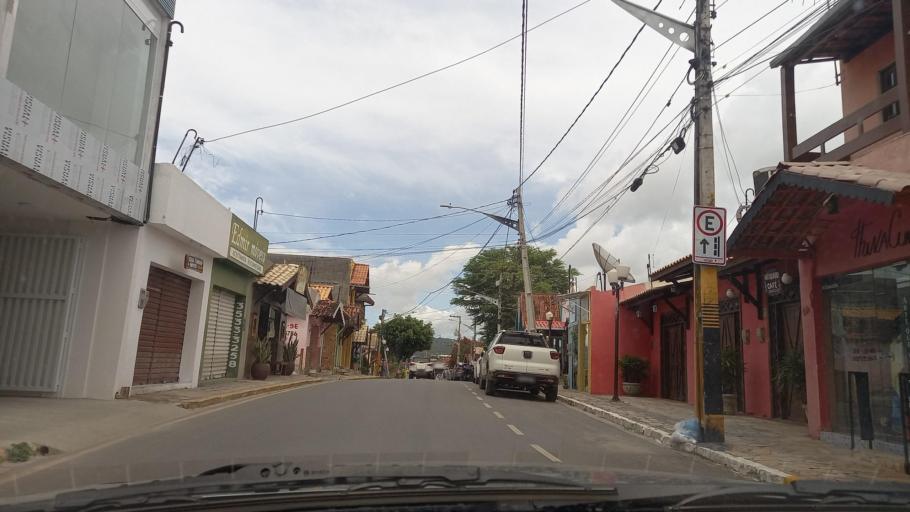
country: BR
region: Pernambuco
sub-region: Gravata
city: Gravata
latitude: -8.1963
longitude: -35.5609
